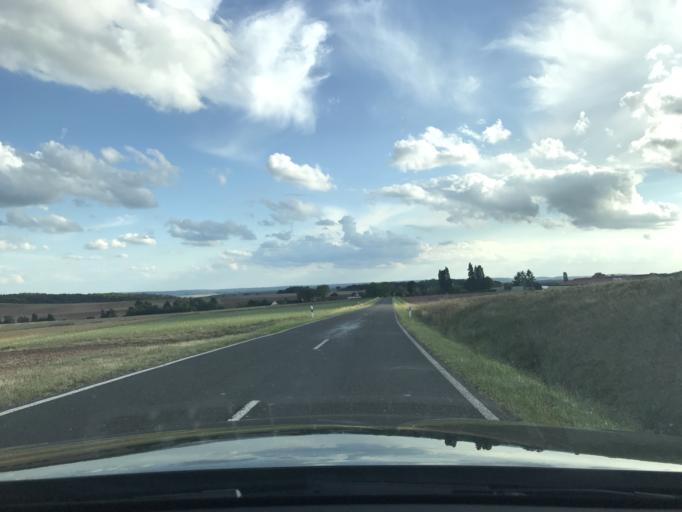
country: DE
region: Bavaria
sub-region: Regierungsbezirk Unterfranken
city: Kirchlauter
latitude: 50.0662
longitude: 10.6758
